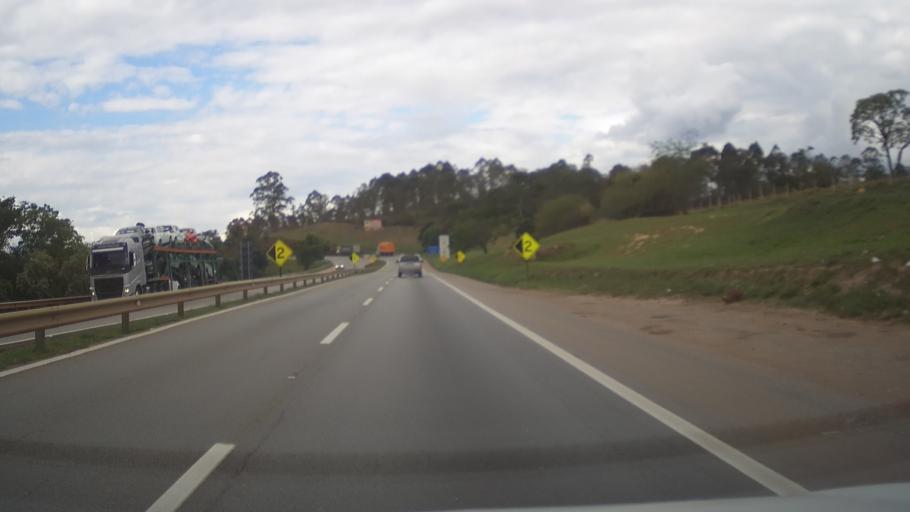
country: BR
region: Minas Gerais
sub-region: Itauna
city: Itauna
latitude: -20.3019
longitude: -44.4435
